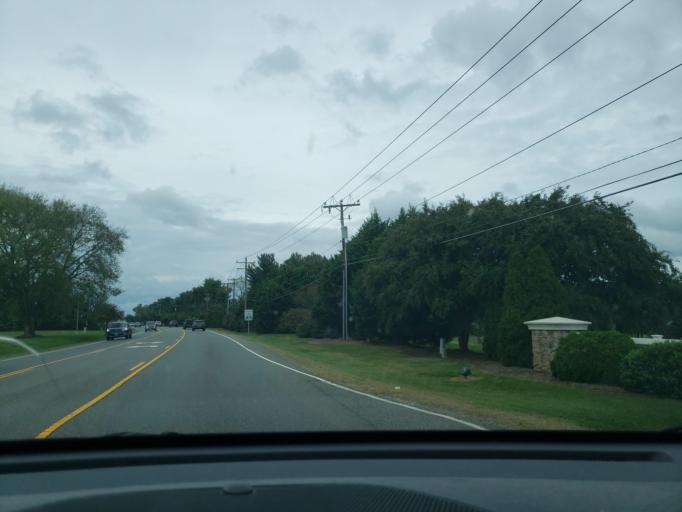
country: US
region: Virginia
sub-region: City of Fredericksburg
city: Fredericksburg
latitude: 38.2605
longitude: -77.4339
